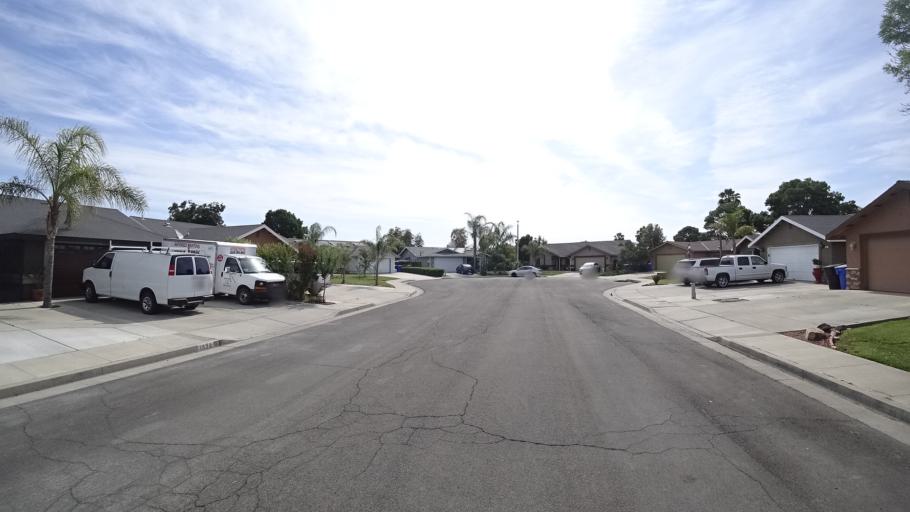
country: US
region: California
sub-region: Kings County
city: Hanford
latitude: 36.3122
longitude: -119.6649
